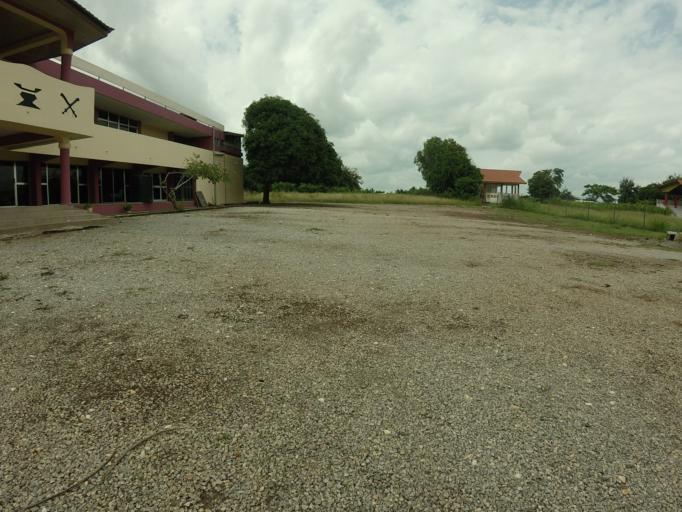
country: GH
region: Volta
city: Ho
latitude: 6.5950
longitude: 0.4643
